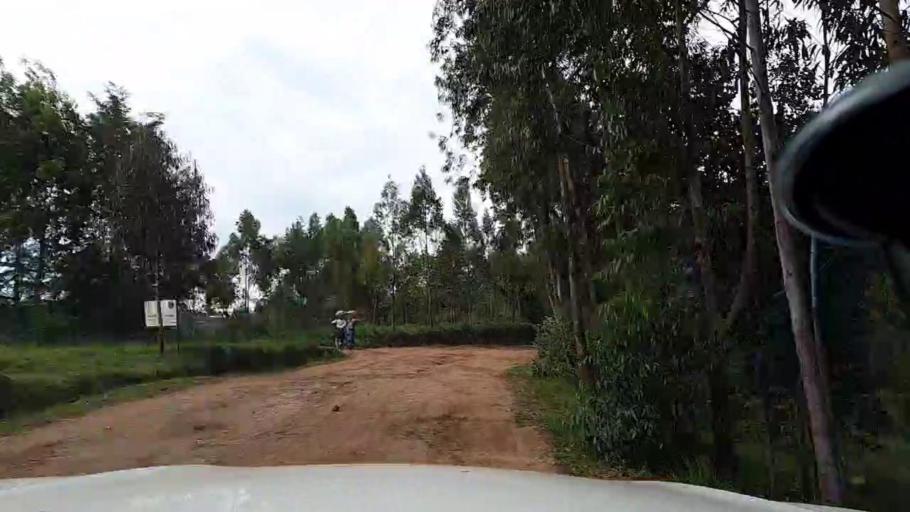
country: RW
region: Kigali
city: Kigali
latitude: -1.7891
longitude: 29.8283
